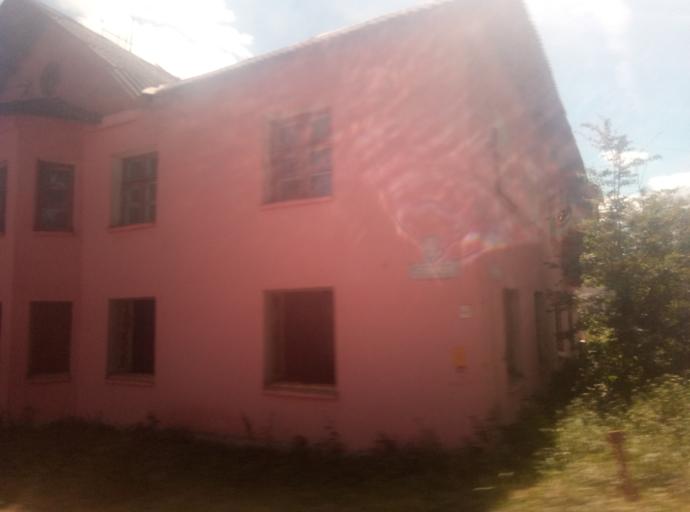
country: RU
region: Tula
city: Kireyevsk
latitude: 53.9280
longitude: 37.9215
